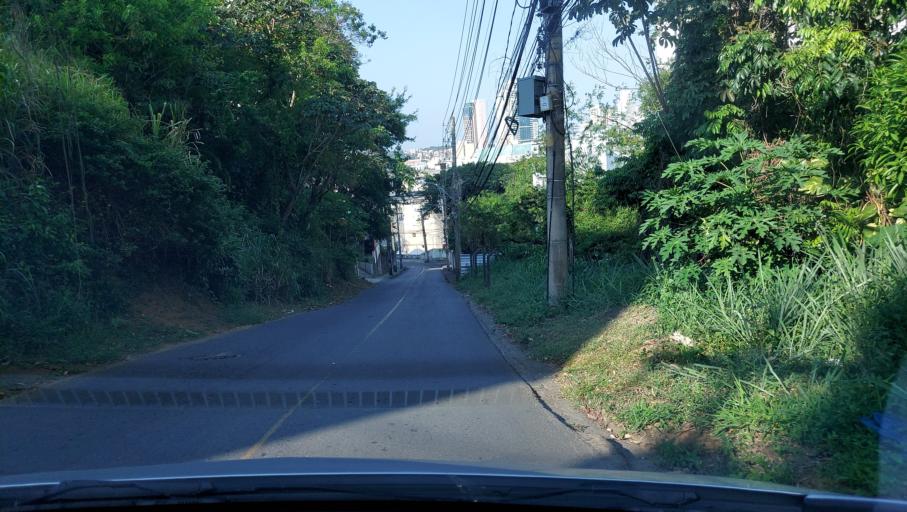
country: BR
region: Bahia
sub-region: Salvador
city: Salvador
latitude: -12.9852
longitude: -38.4703
